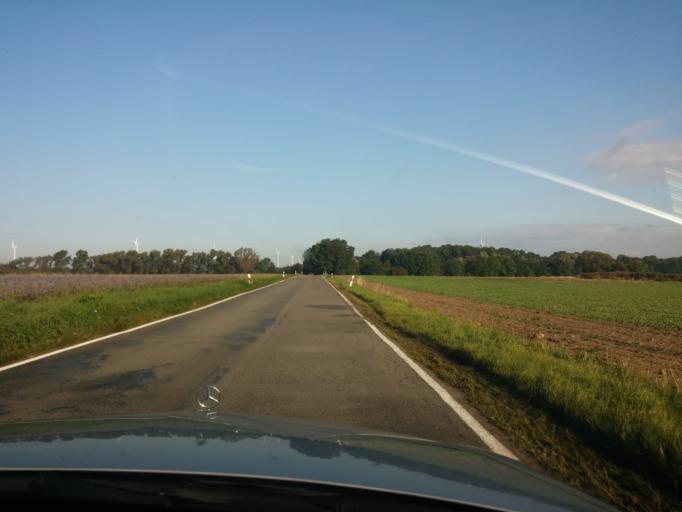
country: DE
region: Brandenburg
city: Putlitz
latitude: 53.3031
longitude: 12.0458
